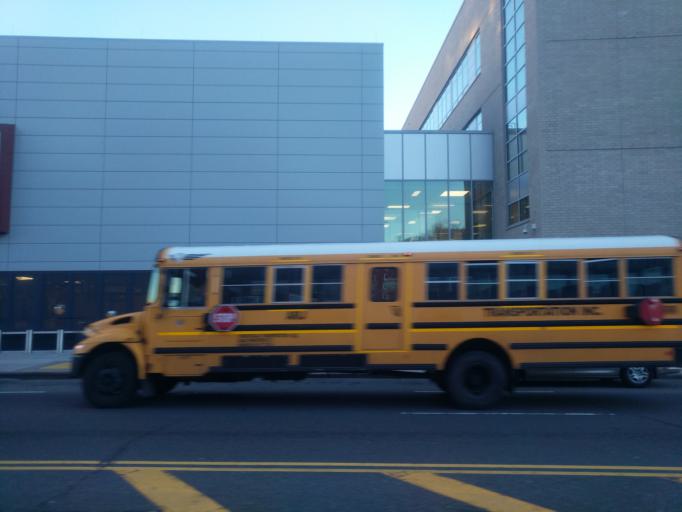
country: US
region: New York
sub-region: Queens County
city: Jamaica
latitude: 40.7088
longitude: -73.7984
